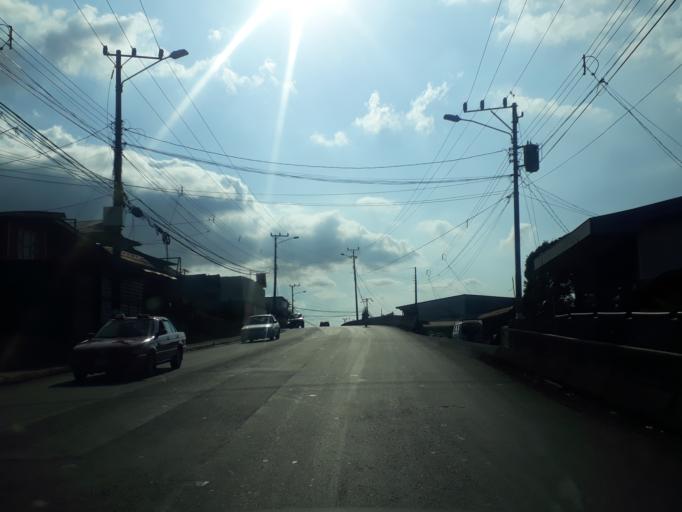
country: CR
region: San Jose
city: Purral
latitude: 9.9668
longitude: -84.0349
